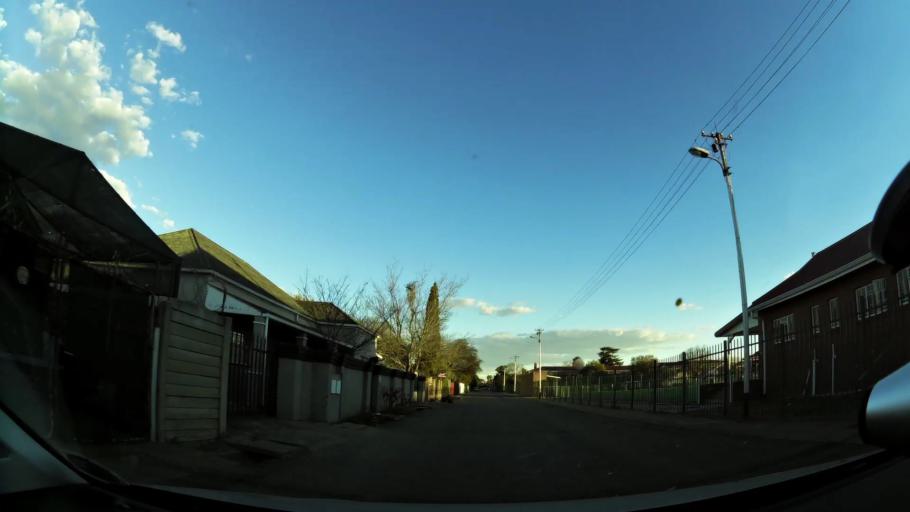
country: ZA
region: North-West
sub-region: Dr Kenneth Kaunda District Municipality
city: Potchefstroom
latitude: -26.7175
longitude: 27.0917
